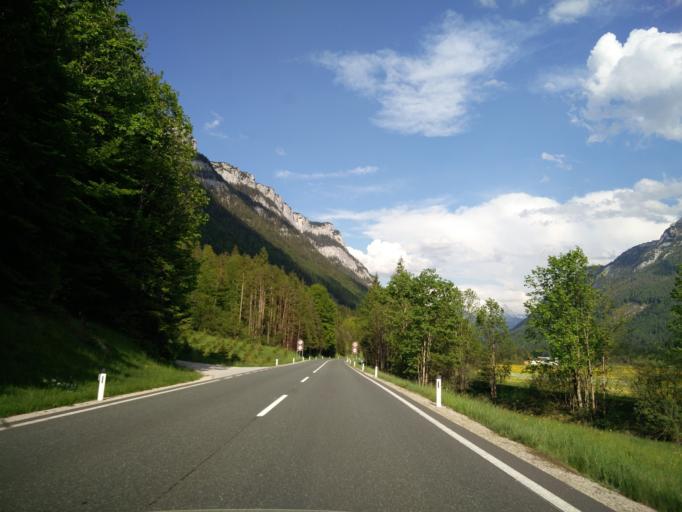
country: AT
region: Tyrol
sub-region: Politischer Bezirk Kitzbuhel
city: Waidring
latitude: 47.5876
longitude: 12.6060
